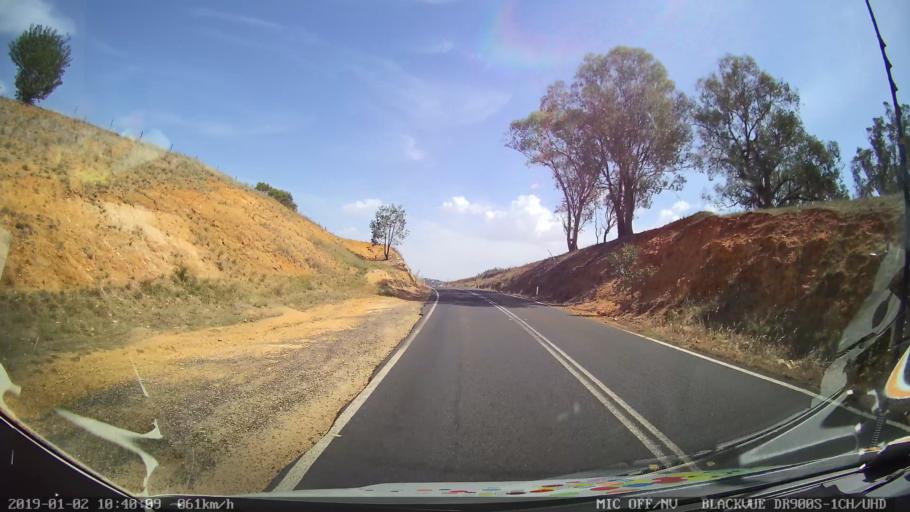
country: AU
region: New South Wales
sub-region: Cootamundra
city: Cootamundra
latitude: -34.8044
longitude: 148.3173
